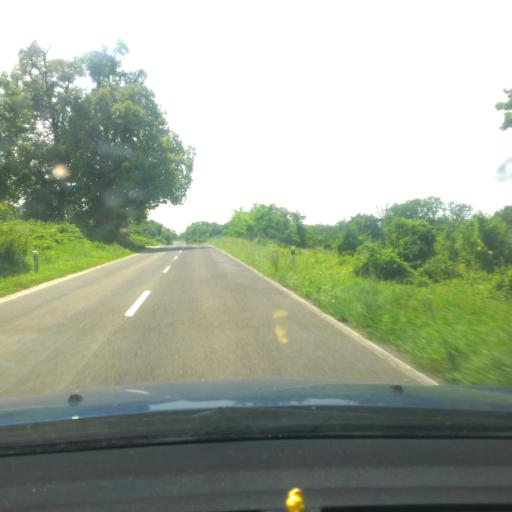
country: SK
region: Trnavsky
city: Hlohovec
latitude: 48.4886
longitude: 17.8116
